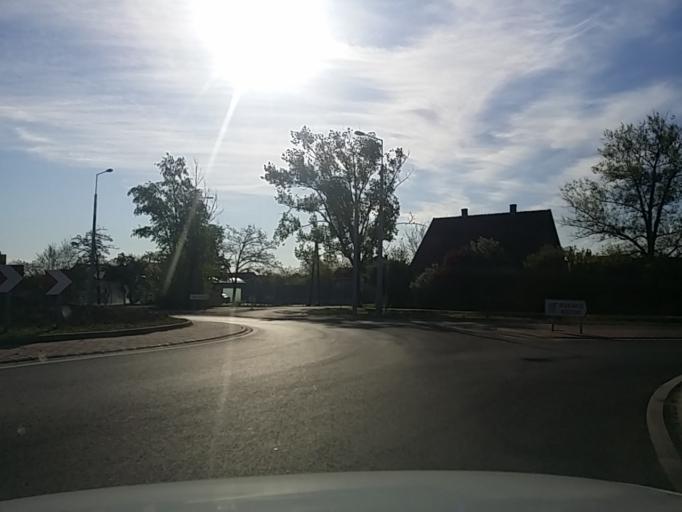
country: HU
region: Jasz-Nagykun-Szolnok
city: Torokszentmiklos
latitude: 47.1738
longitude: 20.3800
